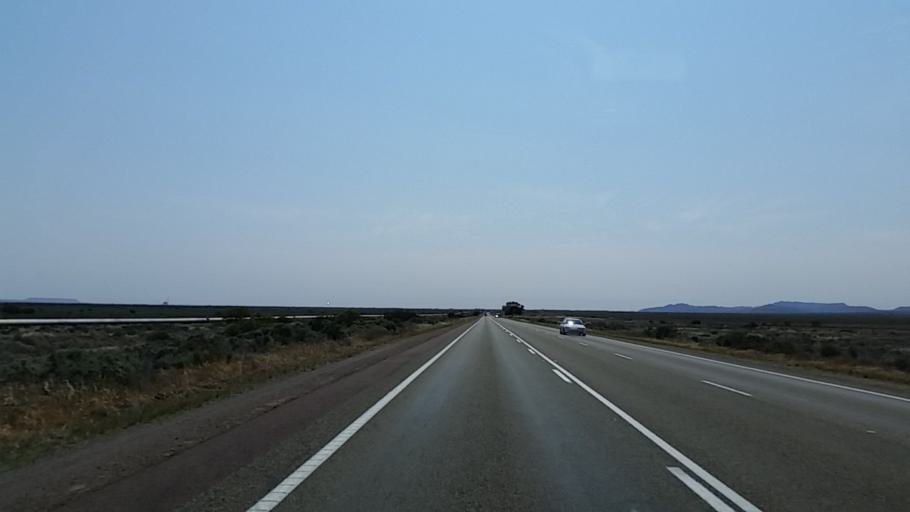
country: AU
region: South Australia
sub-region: Port Augusta
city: Port Augusta
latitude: -32.6774
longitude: 137.9361
